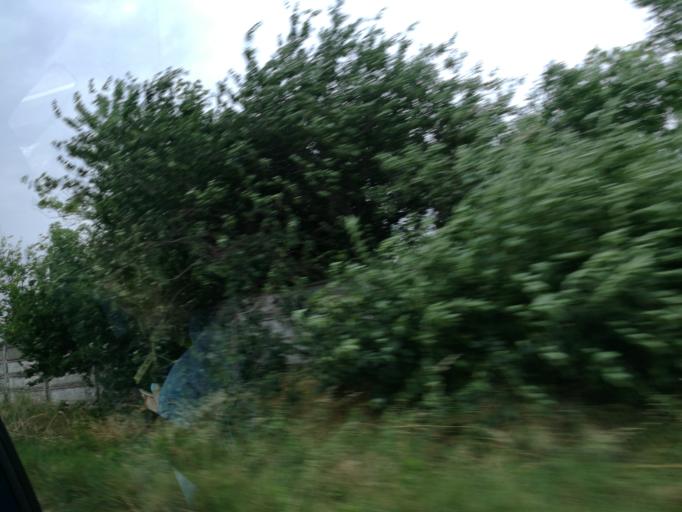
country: RO
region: Constanta
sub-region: Municipiul Mangalia
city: Mangalia
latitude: 43.7801
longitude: 28.5782
